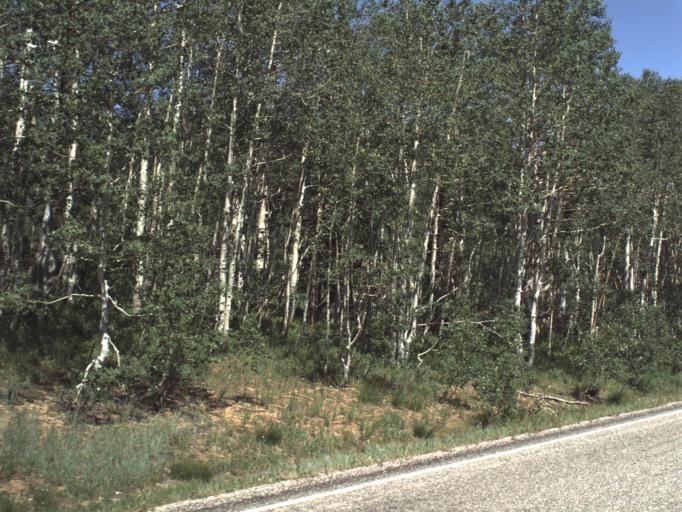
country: US
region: Utah
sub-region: Weber County
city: Wolf Creek
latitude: 41.4428
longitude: -111.5065
